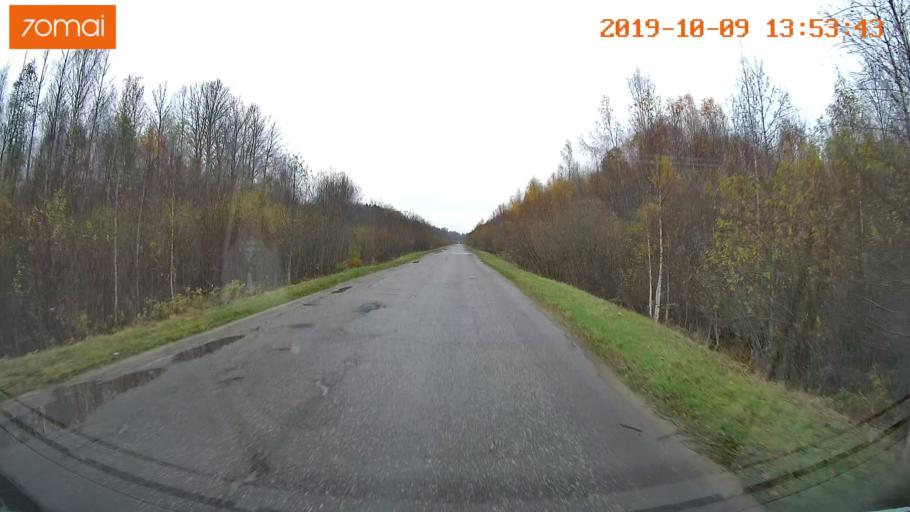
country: RU
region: Kostroma
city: Buy
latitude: 58.4173
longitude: 41.2612
